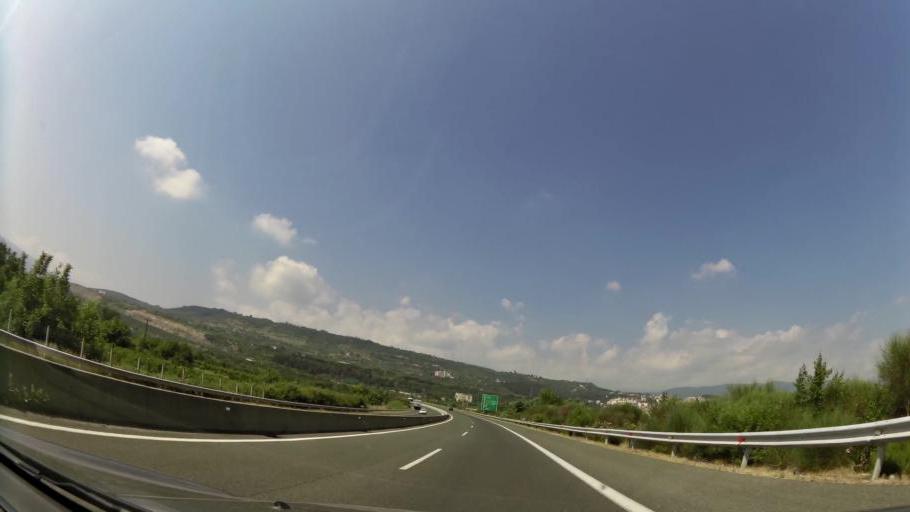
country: GR
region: Central Macedonia
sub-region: Nomos Imathias
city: Veroia
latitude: 40.5129
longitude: 22.2353
